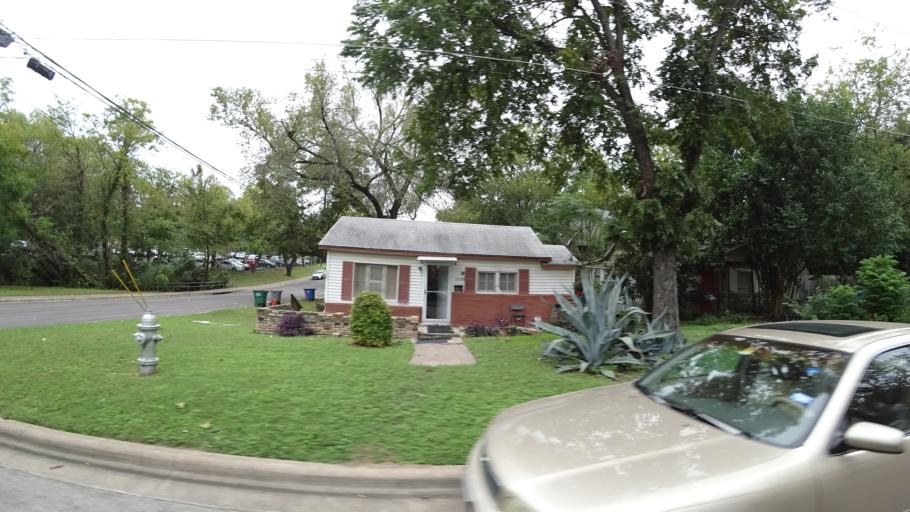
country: US
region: Texas
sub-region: Travis County
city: Austin
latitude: 30.2813
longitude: -97.7196
